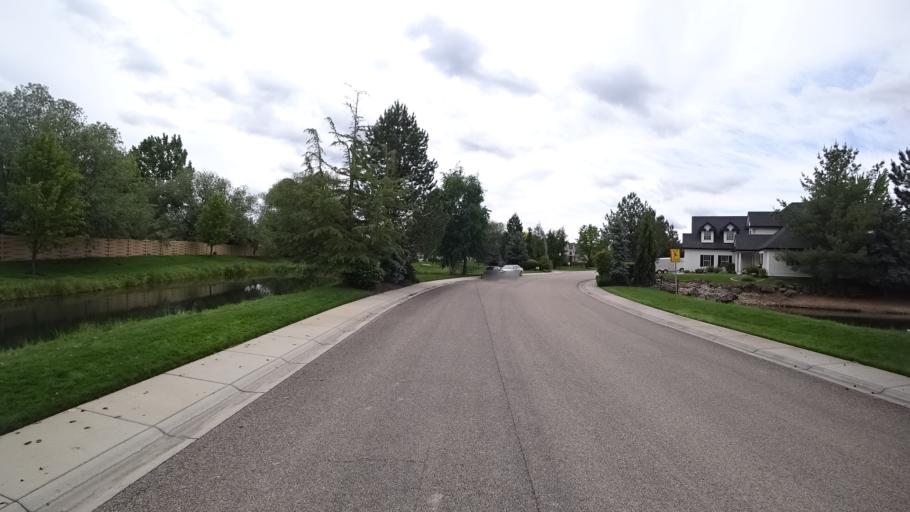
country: US
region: Idaho
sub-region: Ada County
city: Eagle
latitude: 43.6792
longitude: -116.3137
